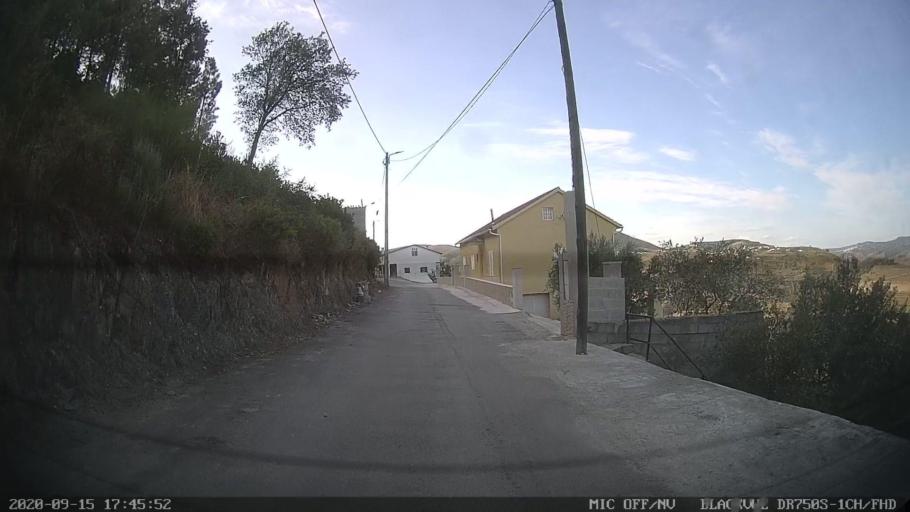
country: PT
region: Vila Real
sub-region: Sabrosa
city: Vilela
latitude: 41.1930
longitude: -7.5703
